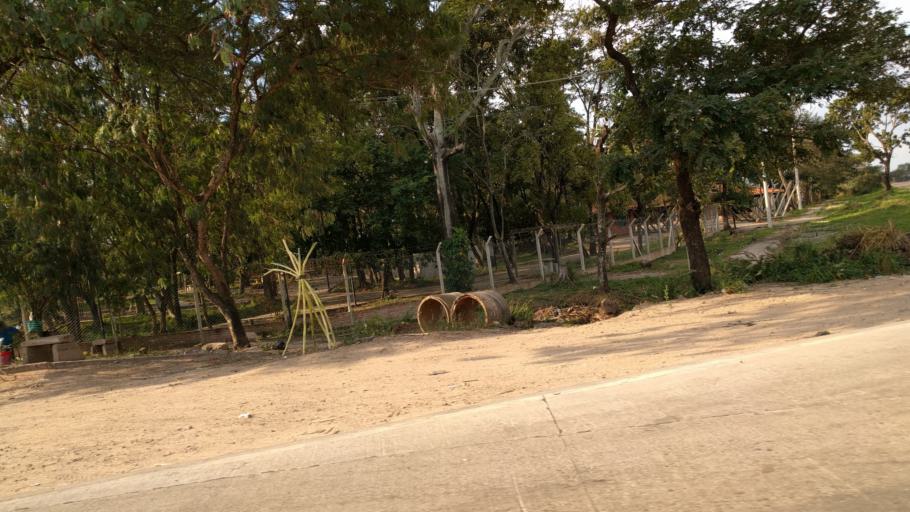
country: BO
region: Santa Cruz
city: Warnes
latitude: -17.5063
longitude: -63.1695
